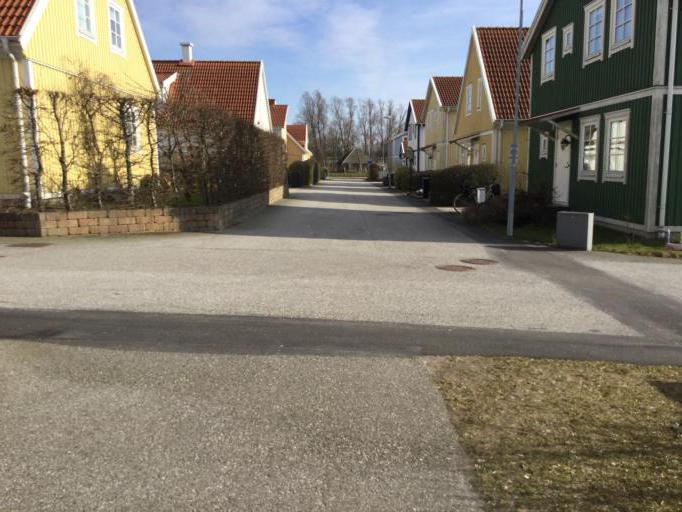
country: SE
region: Skane
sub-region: Lunds Kommun
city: Lund
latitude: 55.7306
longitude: 13.1919
